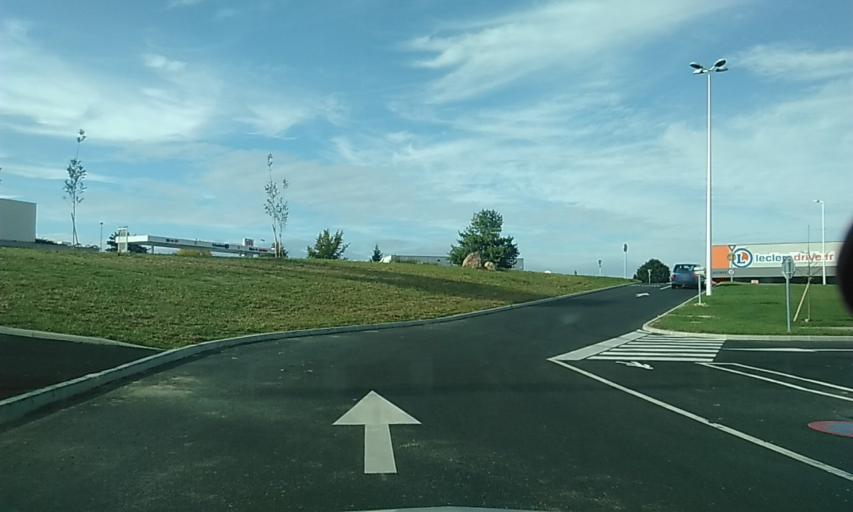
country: FR
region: Brittany
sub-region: Departement d'Ille-et-Vilaine
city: Pleumeleuc
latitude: 48.1767
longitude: -1.9182
